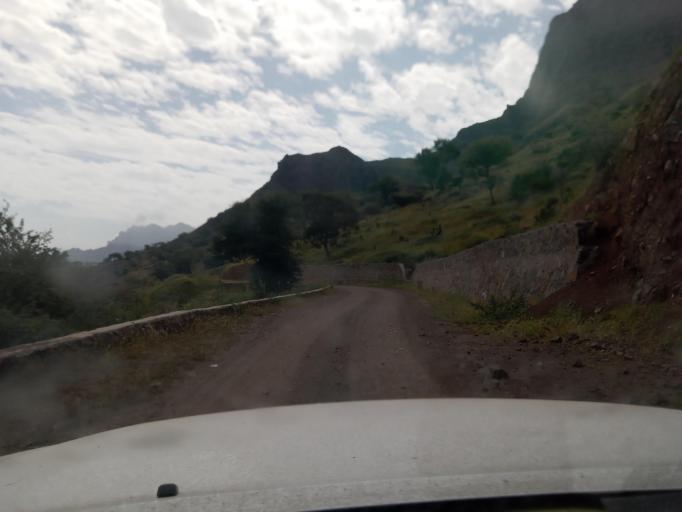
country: CV
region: Santa Catarina
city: Assomada
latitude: 15.0822
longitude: -23.7079
